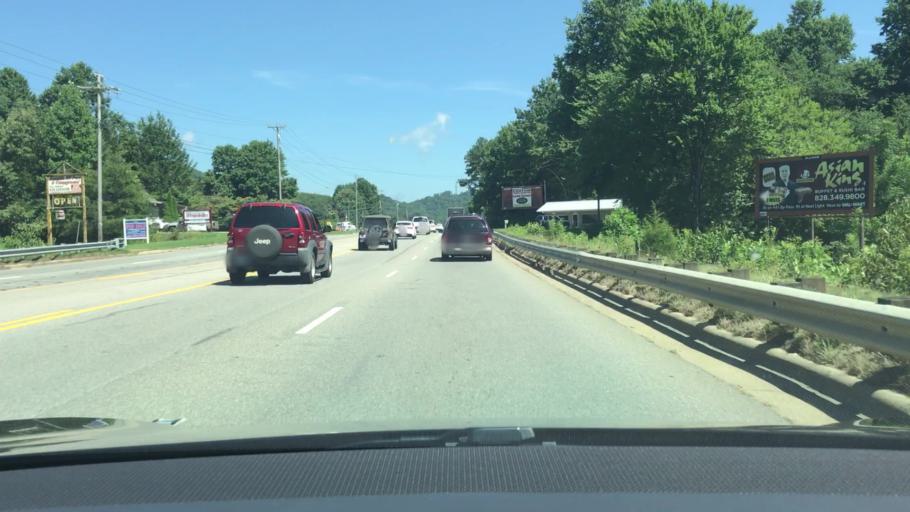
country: US
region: North Carolina
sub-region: Macon County
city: Franklin
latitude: 35.1234
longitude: -83.3935
